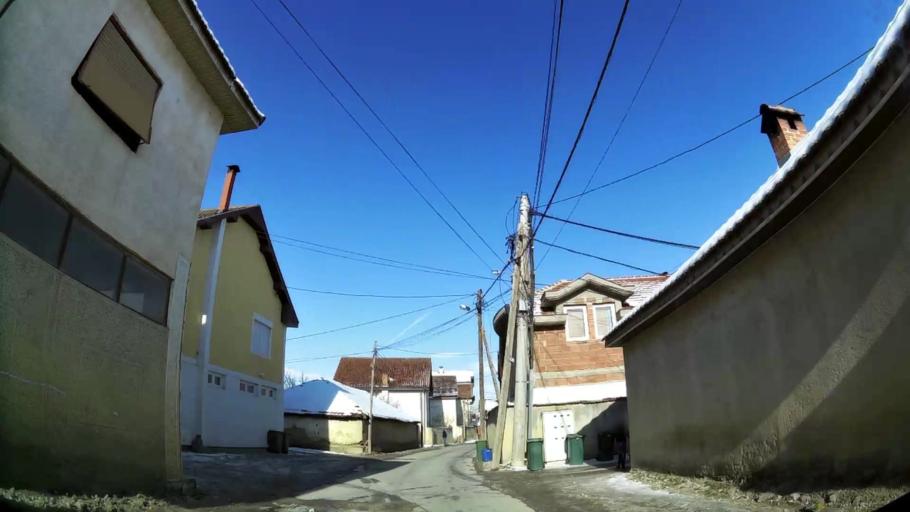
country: MK
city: Grchec
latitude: 41.9893
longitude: 21.3306
